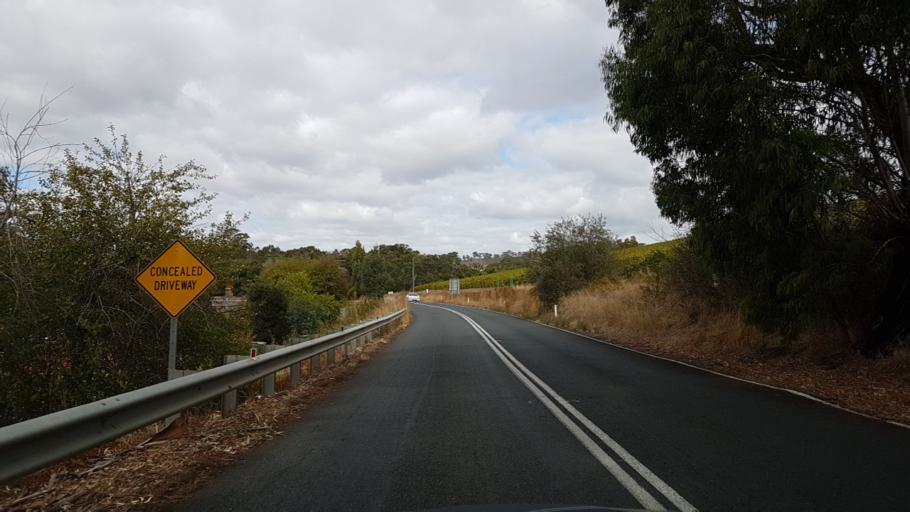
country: AU
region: South Australia
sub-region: Adelaide Hills
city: Gumeracha
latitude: -34.8204
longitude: 138.8738
